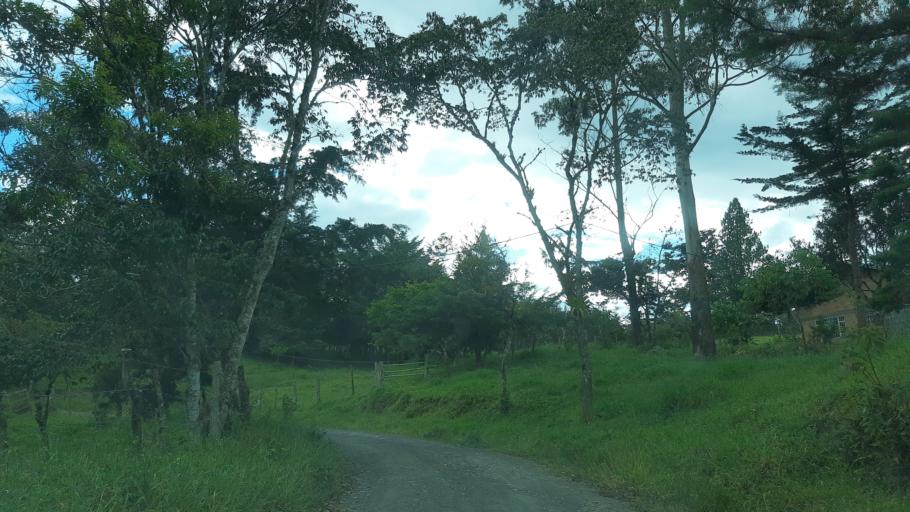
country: CO
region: Boyaca
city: Garagoa
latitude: 5.0189
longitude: -73.3326
